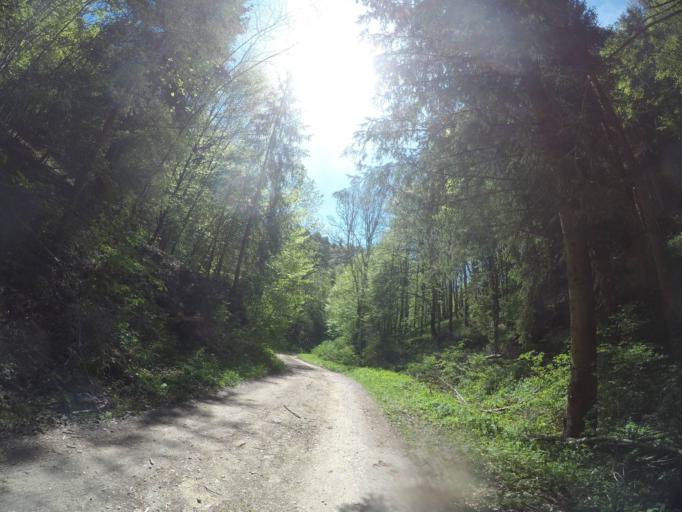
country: DE
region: Baden-Wuerttemberg
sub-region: Tuebingen Region
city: Laichingen
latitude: 48.4305
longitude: 9.6833
